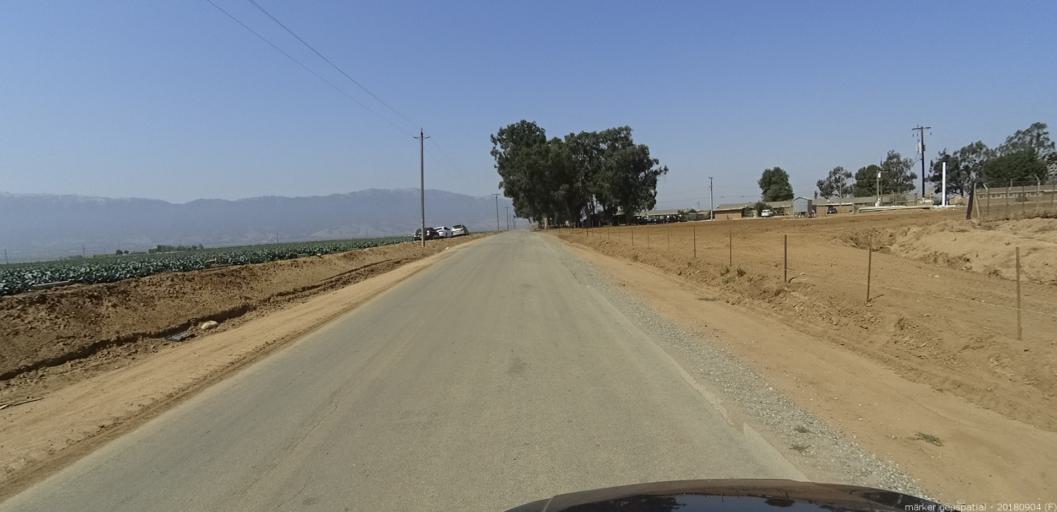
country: US
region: California
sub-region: Monterey County
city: Chualar
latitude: 36.5572
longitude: -121.4711
